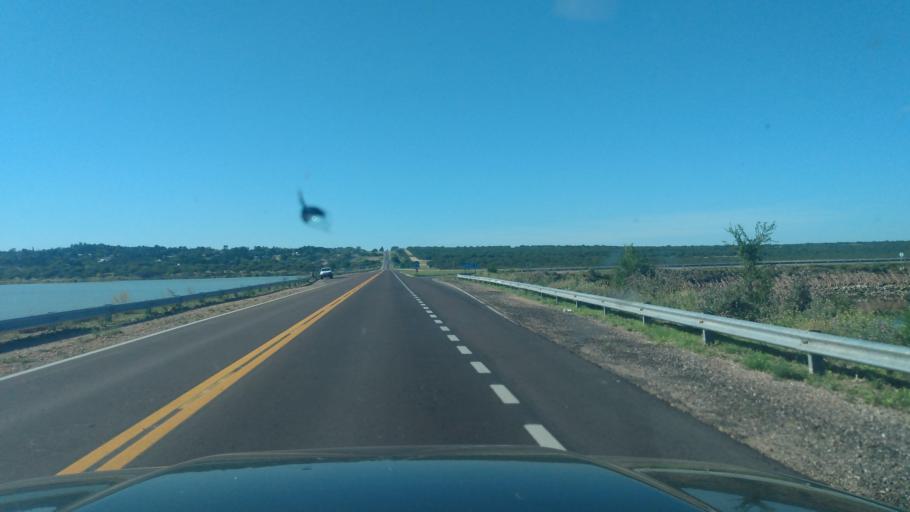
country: AR
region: La Pampa
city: Santa Rosa
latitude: -36.7142
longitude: -64.2831
